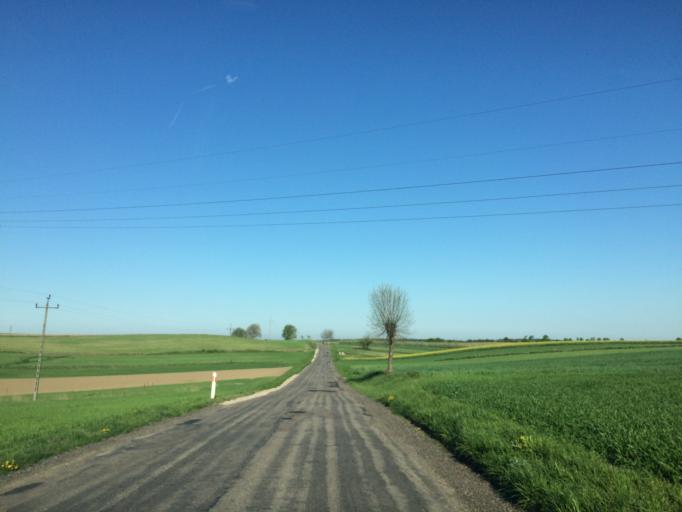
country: PL
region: Warmian-Masurian Voivodeship
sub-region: Powiat dzialdowski
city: Rybno
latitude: 53.3988
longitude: 19.8668
